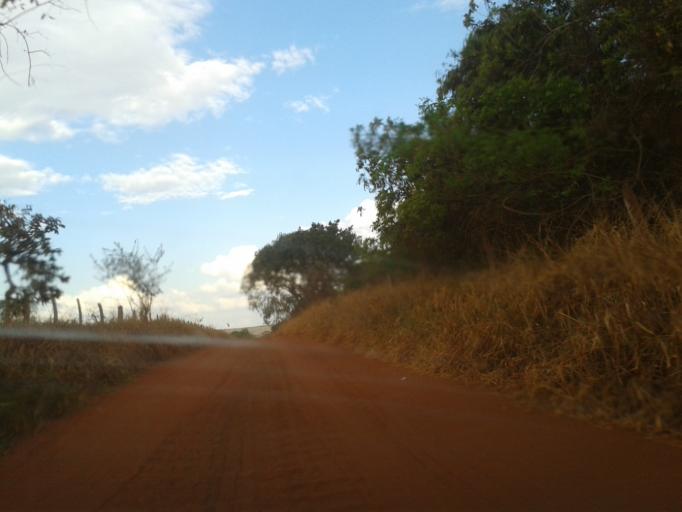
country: BR
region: Minas Gerais
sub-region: Ituiutaba
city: Ituiutaba
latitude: -19.2022
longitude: -49.8133
